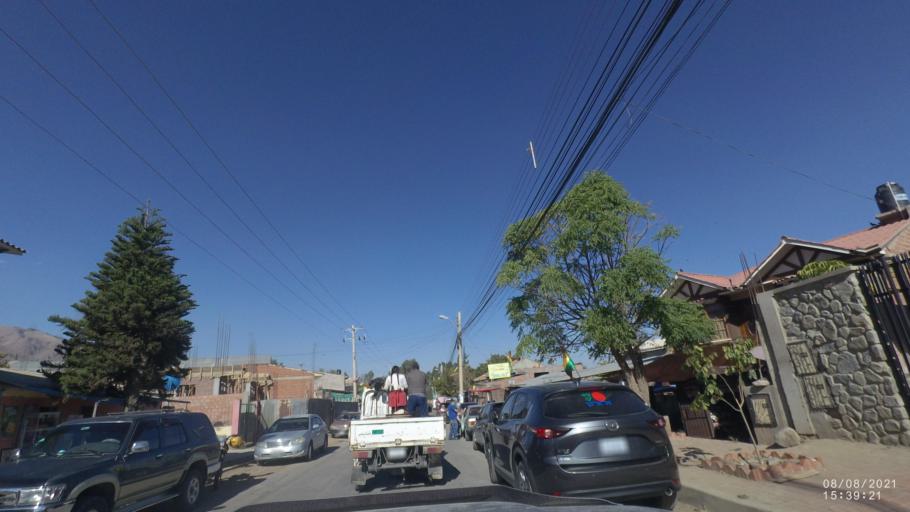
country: BO
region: Cochabamba
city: Cochabamba
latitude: -17.3354
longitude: -66.2324
